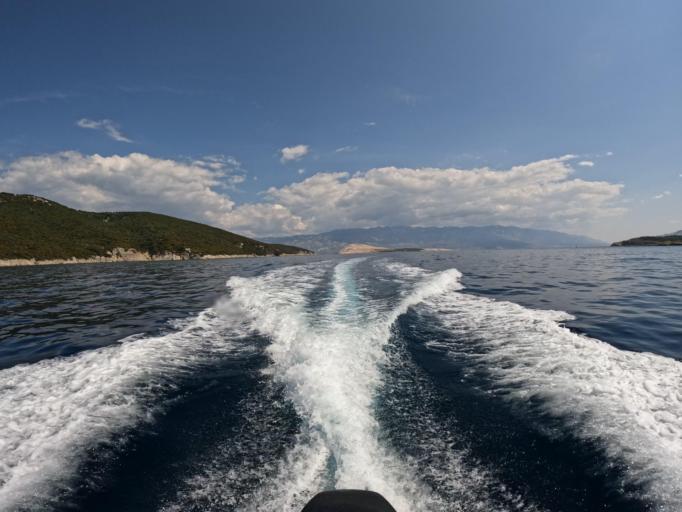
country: HR
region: Primorsko-Goranska
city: Lopar
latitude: 44.8552
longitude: 14.7484
